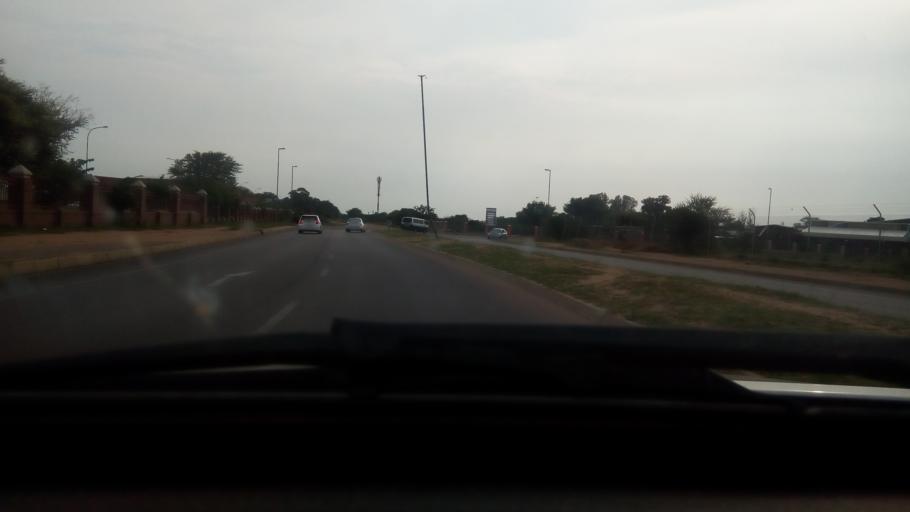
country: BW
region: South East
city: Gaborone
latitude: -24.6655
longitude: 25.9326
